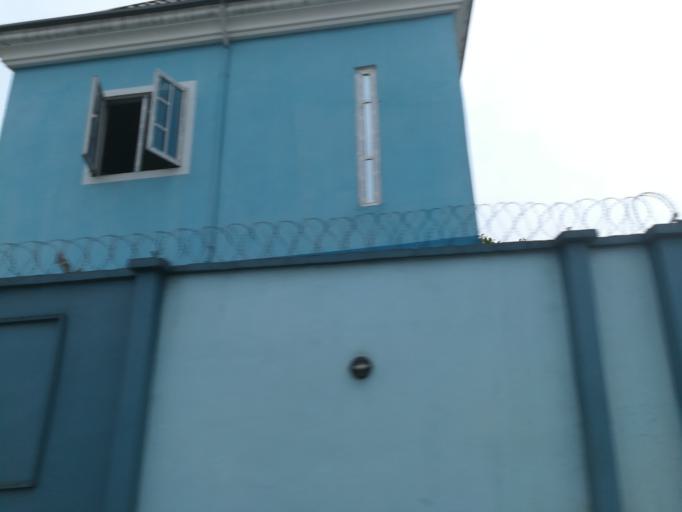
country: NG
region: Rivers
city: Okrika
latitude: 4.7789
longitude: 7.1299
